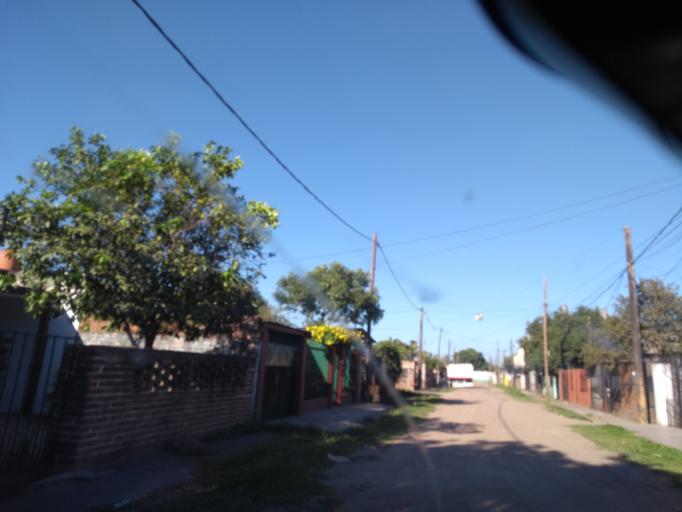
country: AR
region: Chaco
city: Resistencia
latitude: -27.4744
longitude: -58.9702
